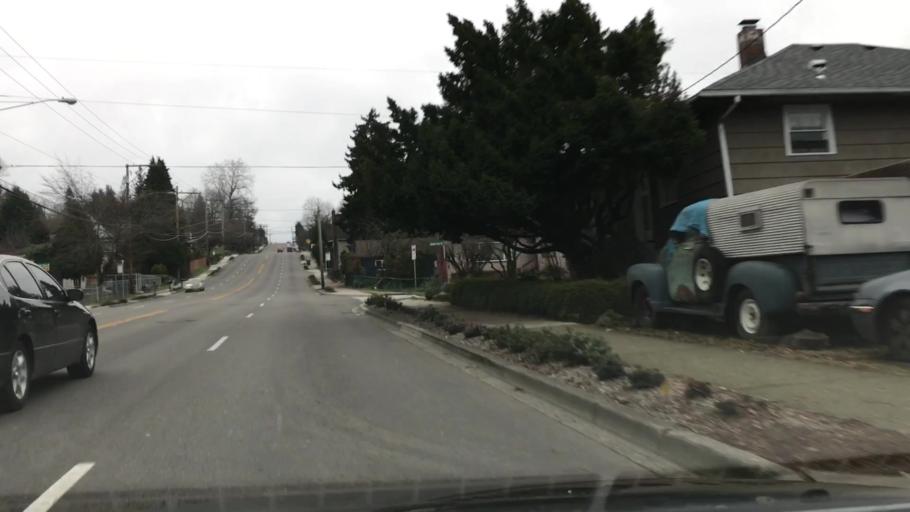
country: US
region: Washington
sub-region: King County
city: Kent
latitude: 47.3866
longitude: -122.2262
